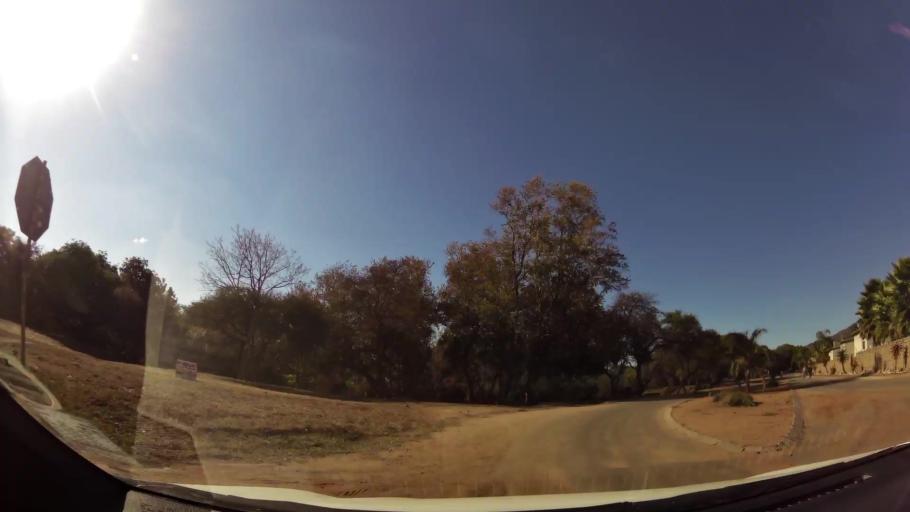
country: ZA
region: Limpopo
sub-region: Waterberg District Municipality
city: Mokopane
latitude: -24.1749
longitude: 29.0138
